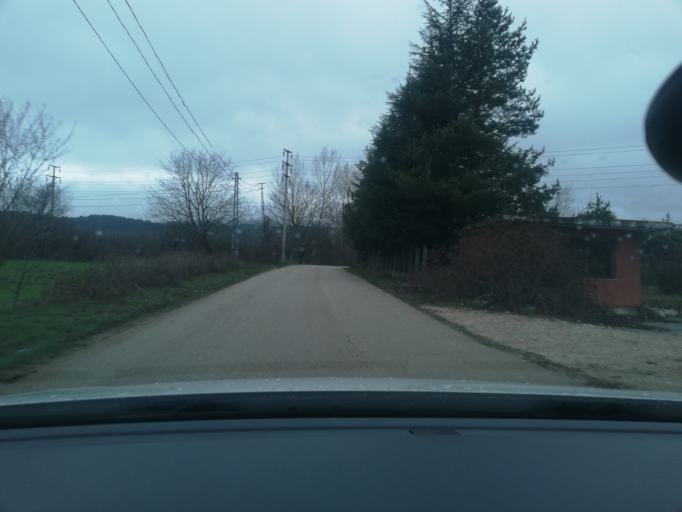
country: TR
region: Bolu
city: Bolu
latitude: 40.7317
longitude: 31.5440
